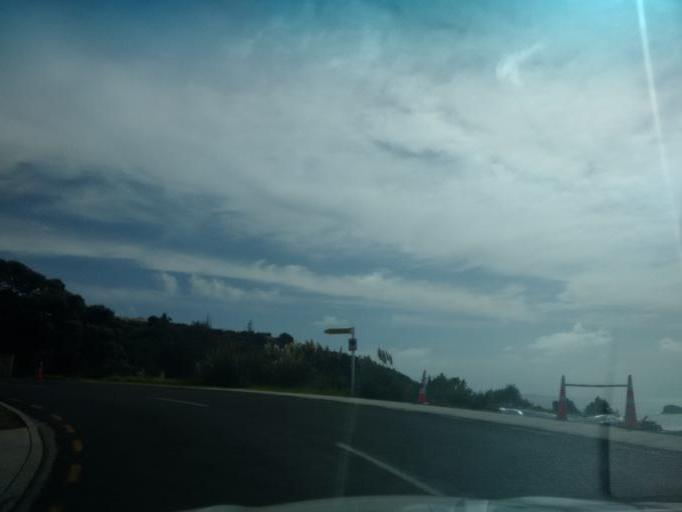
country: NZ
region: Waikato
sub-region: Thames-Coromandel District
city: Whitianga
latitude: -36.8374
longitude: 175.8006
